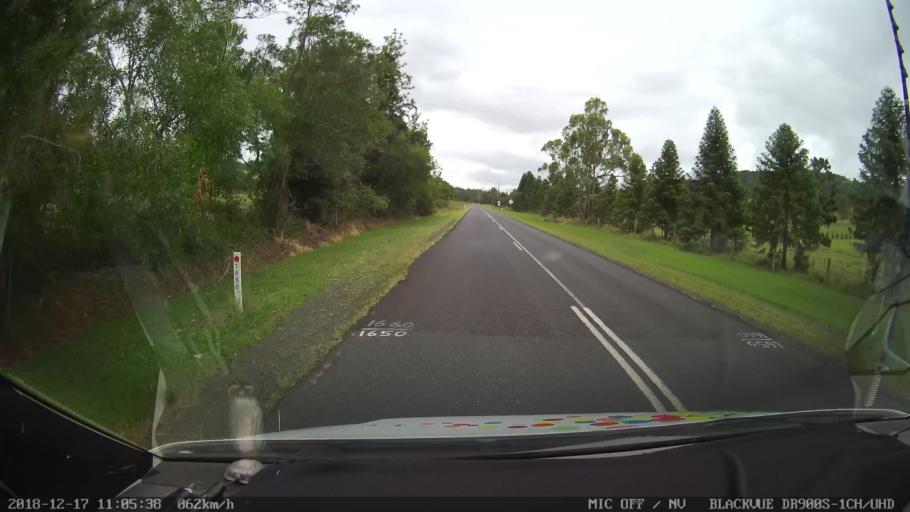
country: AU
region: New South Wales
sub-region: Kyogle
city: Kyogle
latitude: -28.7886
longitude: 152.6478
